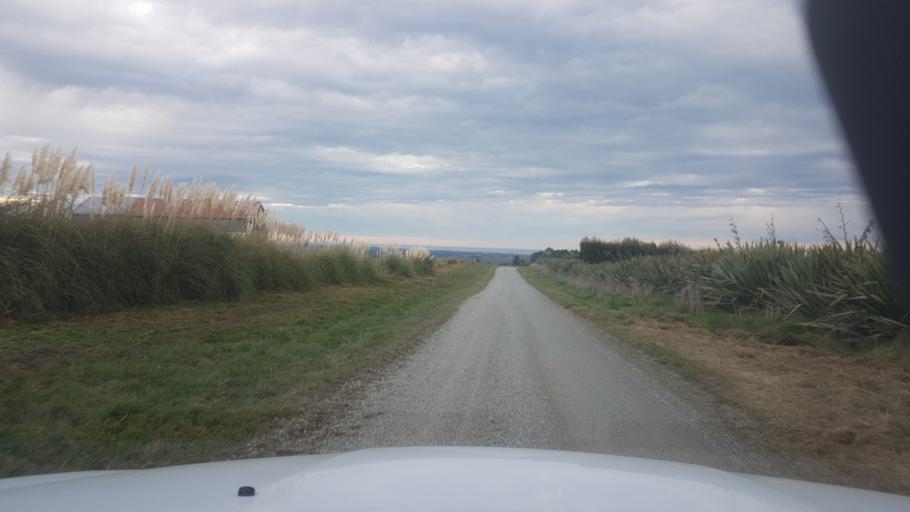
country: NZ
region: Canterbury
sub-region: Timaru District
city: Pleasant Point
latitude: -44.3458
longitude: 171.1235
